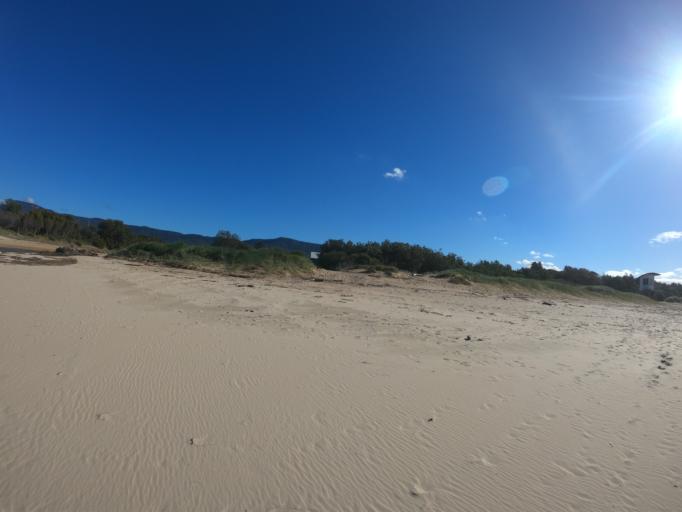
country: AU
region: New South Wales
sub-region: Wollongong
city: East Corrimal
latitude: -34.3828
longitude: 150.9161
